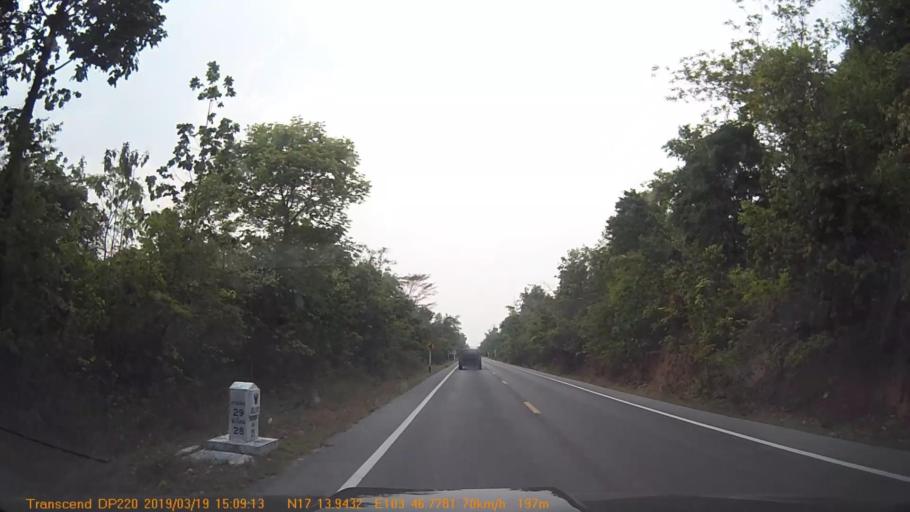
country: TH
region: Sakon Nakhon
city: Nikhom Nam Un
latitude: 17.2324
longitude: 103.7795
